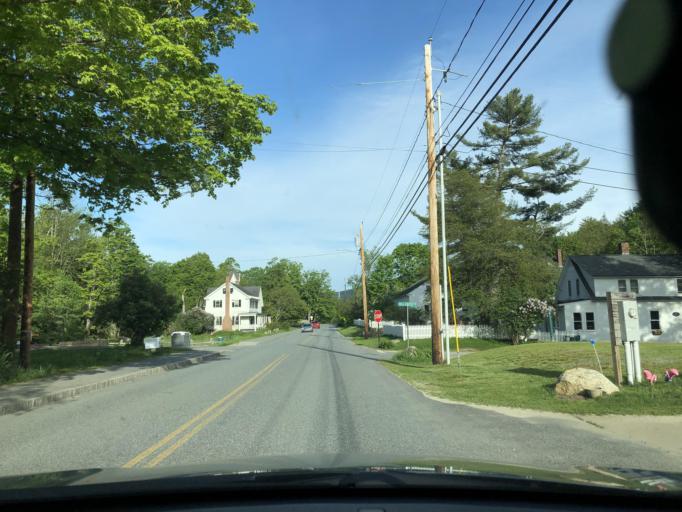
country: US
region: New Hampshire
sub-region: Merrimack County
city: Wilmot
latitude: 43.4196
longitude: -71.9372
